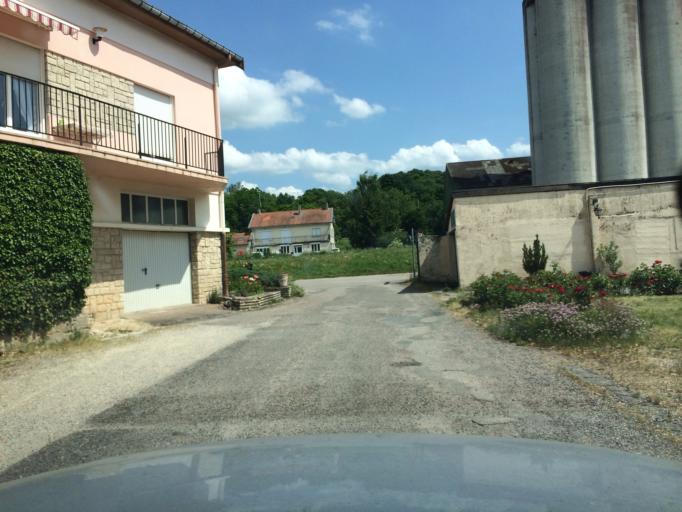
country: FR
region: Lorraine
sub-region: Departement de la Meuse
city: Vacon
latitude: 48.6855
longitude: 5.6189
